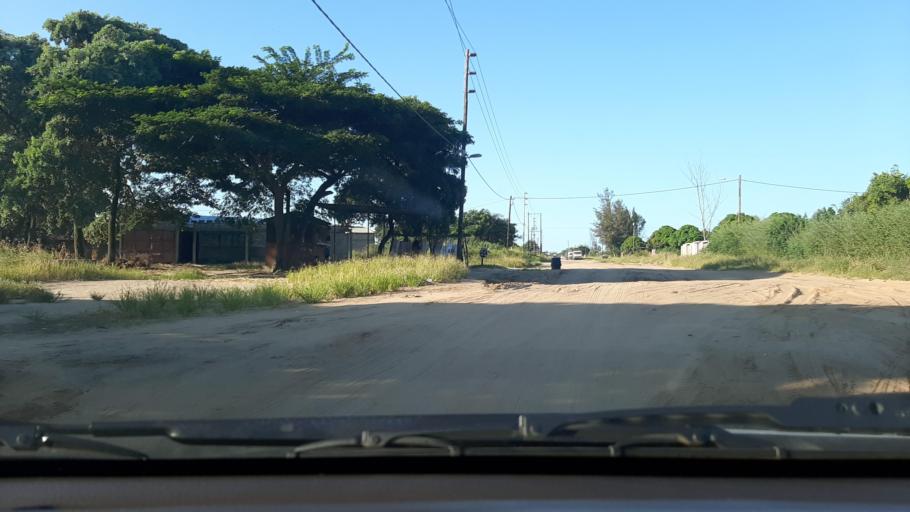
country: MZ
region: Maputo City
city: Maputo
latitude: -25.7617
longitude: 32.5482
